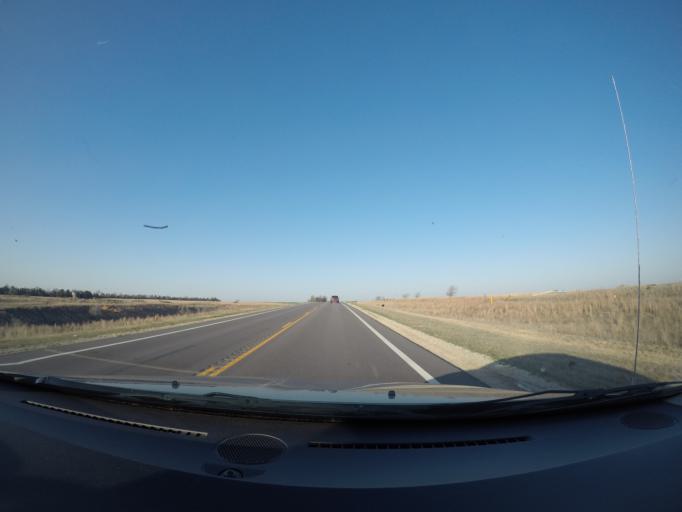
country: US
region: Kansas
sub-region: Pratt County
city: Pratt
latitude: 37.7006
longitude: -98.6778
